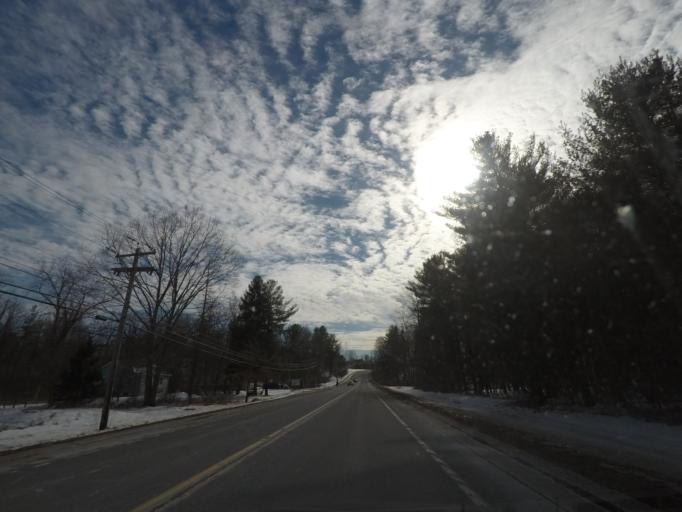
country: US
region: New York
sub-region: Albany County
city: Westmere
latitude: 42.6870
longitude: -73.9011
